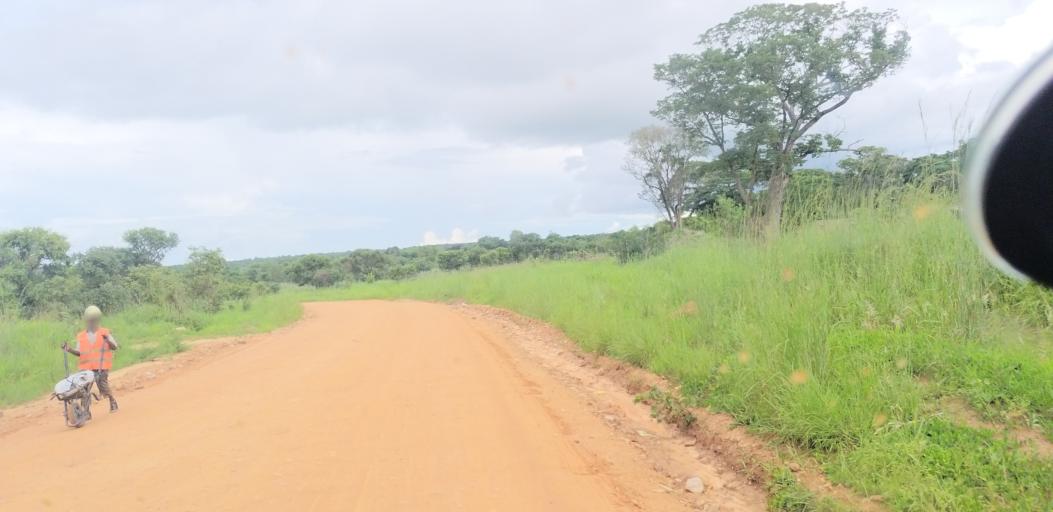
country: ZM
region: Lusaka
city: Lusaka
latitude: -15.1970
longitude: 28.4423
